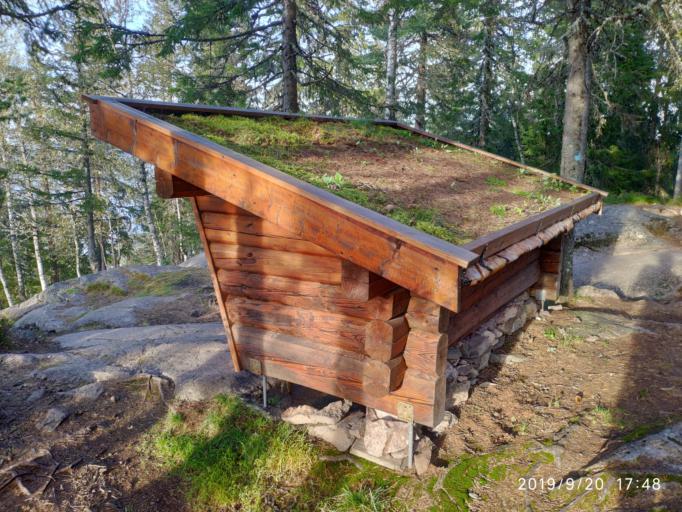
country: NO
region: Buskerud
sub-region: Hole
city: Vik
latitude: 60.0493
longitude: 10.3087
